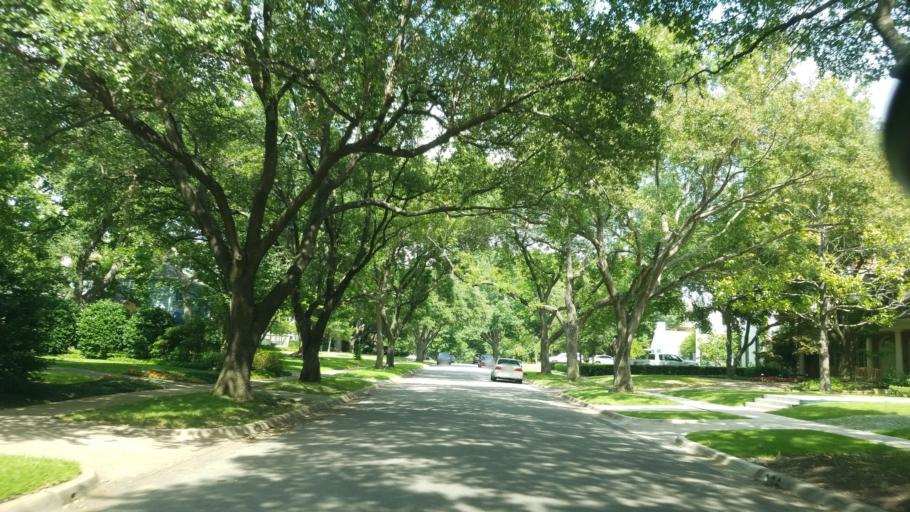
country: US
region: Texas
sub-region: Dallas County
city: University Park
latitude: 32.8581
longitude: -96.7961
